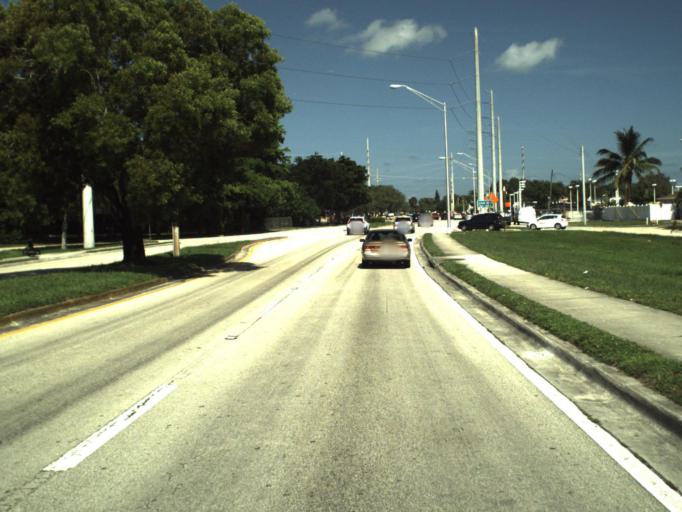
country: US
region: Florida
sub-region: Broward County
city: Pembroke Pines
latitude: 26.0322
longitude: -80.2118
